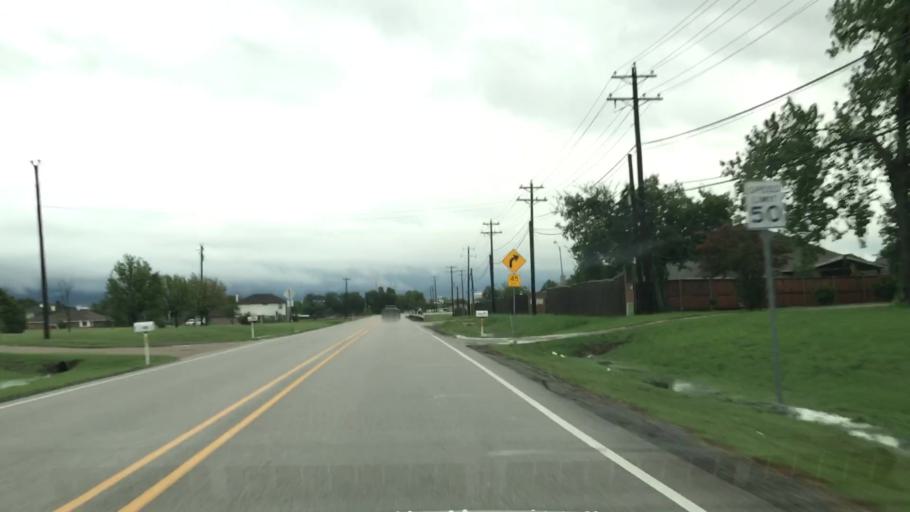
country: US
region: Texas
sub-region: Collin County
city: Wylie
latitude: 33.0278
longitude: -96.5435
